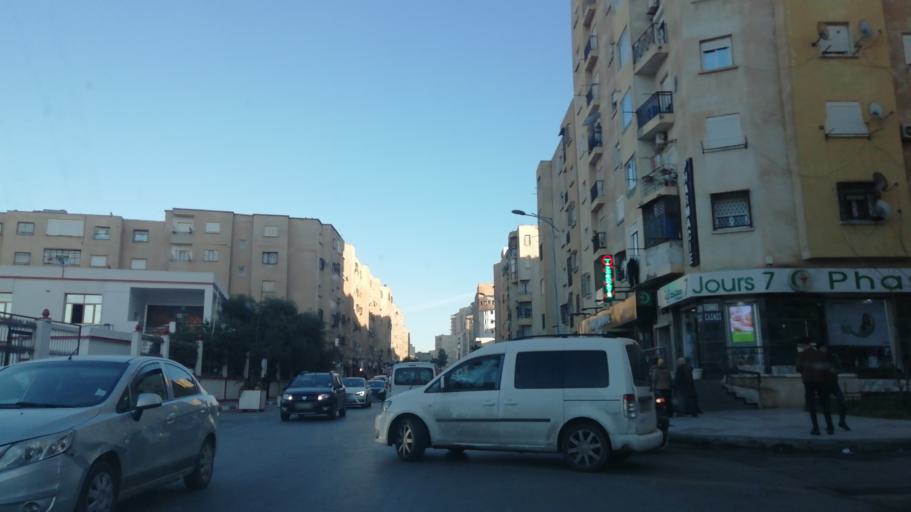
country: DZ
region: Oran
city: Bir el Djir
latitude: 35.7231
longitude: -0.5910
